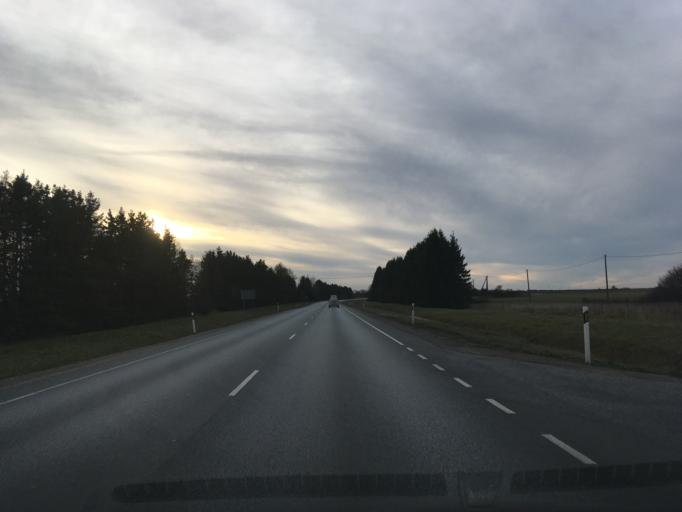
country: EE
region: Ida-Virumaa
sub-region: Kohtla-Nomme vald
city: Kohtla-Nomme
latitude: 59.4138
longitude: 27.1388
